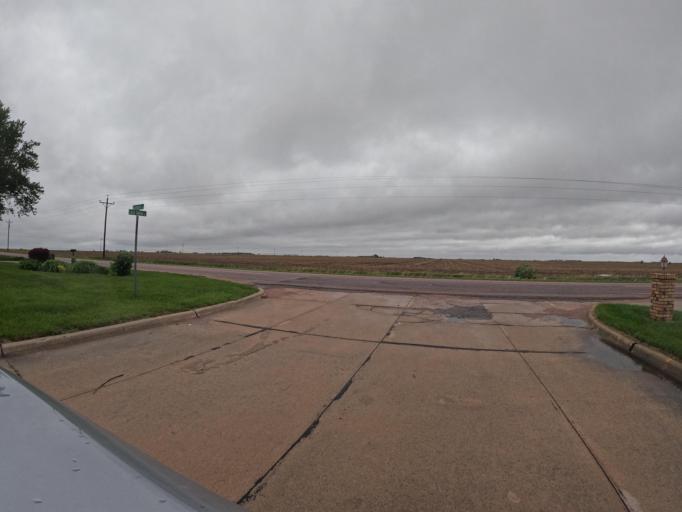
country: US
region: Nebraska
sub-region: Clay County
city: Harvard
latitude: 40.6237
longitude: -98.0899
